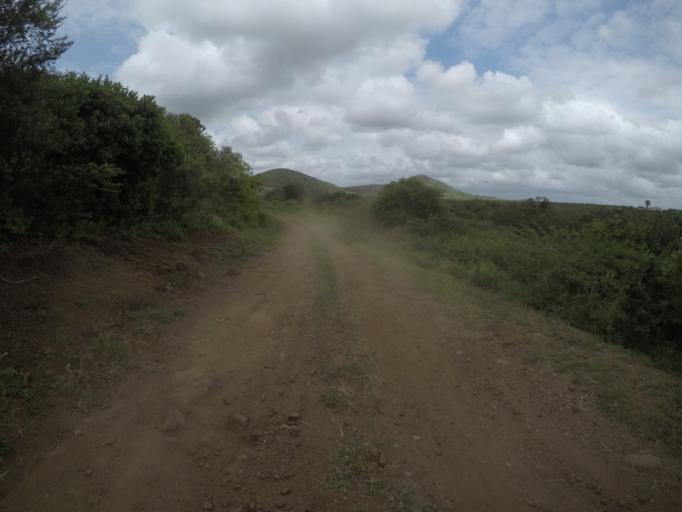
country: ZA
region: KwaZulu-Natal
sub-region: uThungulu District Municipality
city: Empangeni
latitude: -28.5875
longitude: 31.8702
